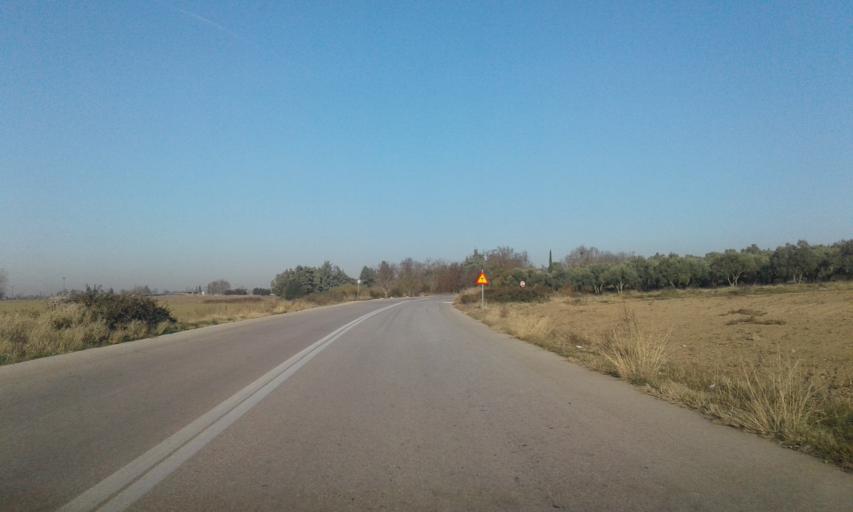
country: GR
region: Central Macedonia
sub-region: Nomos Thessalonikis
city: Kolchikon
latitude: 40.7104
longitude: 23.1807
